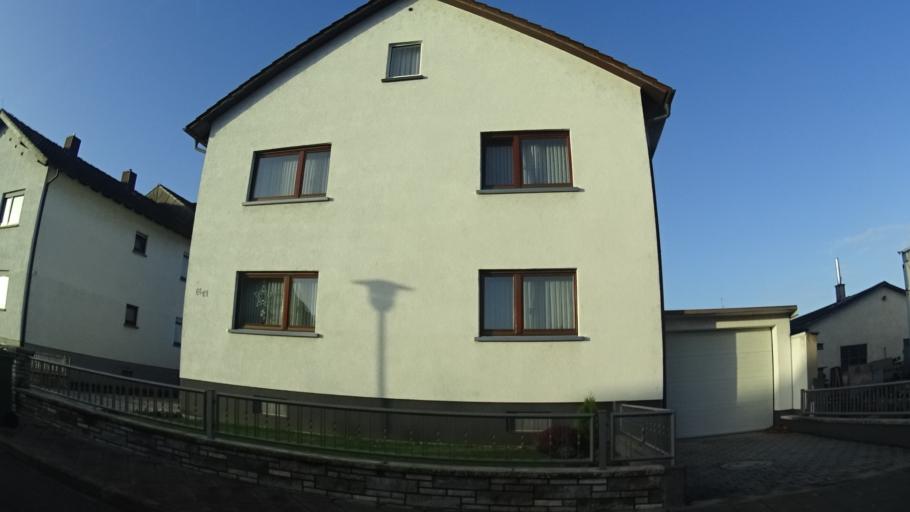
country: DE
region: Baden-Wuerttemberg
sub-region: Karlsruhe Region
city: Forst
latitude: 49.1525
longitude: 8.5781
